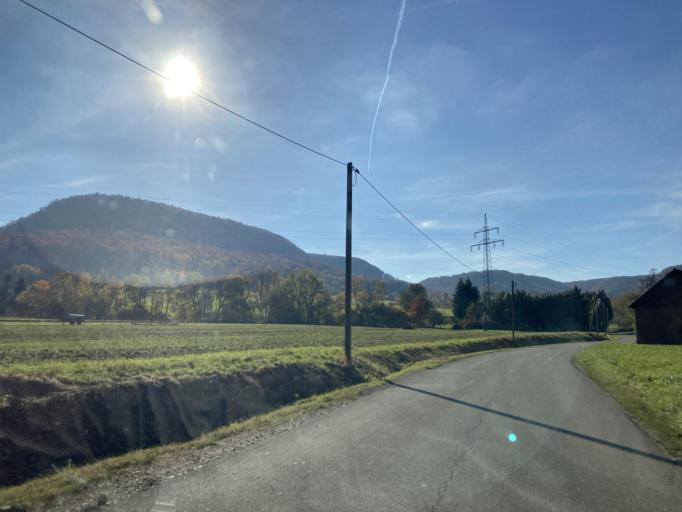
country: DE
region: Baden-Wuerttemberg
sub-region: Tuebingen Region
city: Mossingen
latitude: 48.3791
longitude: 9.1011
